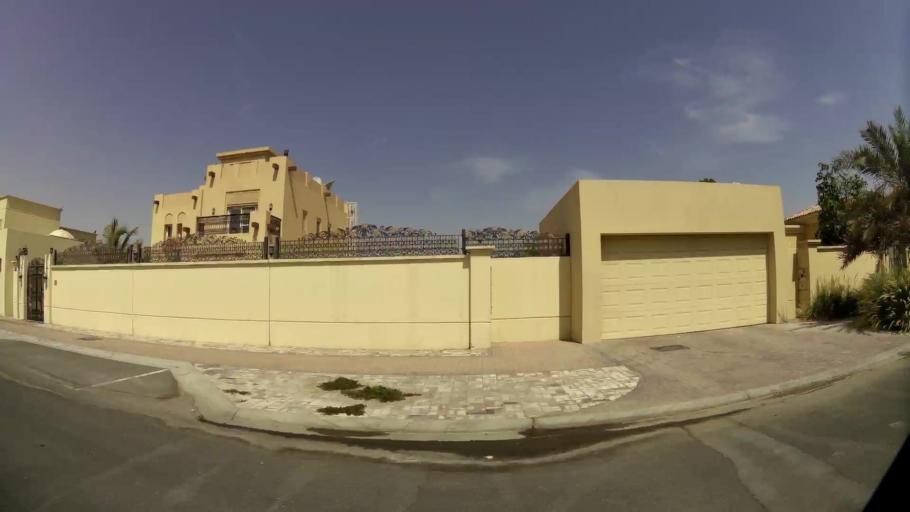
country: AE
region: Ash Shariqah
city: Sharjah
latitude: 25.1870
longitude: 55.4435
